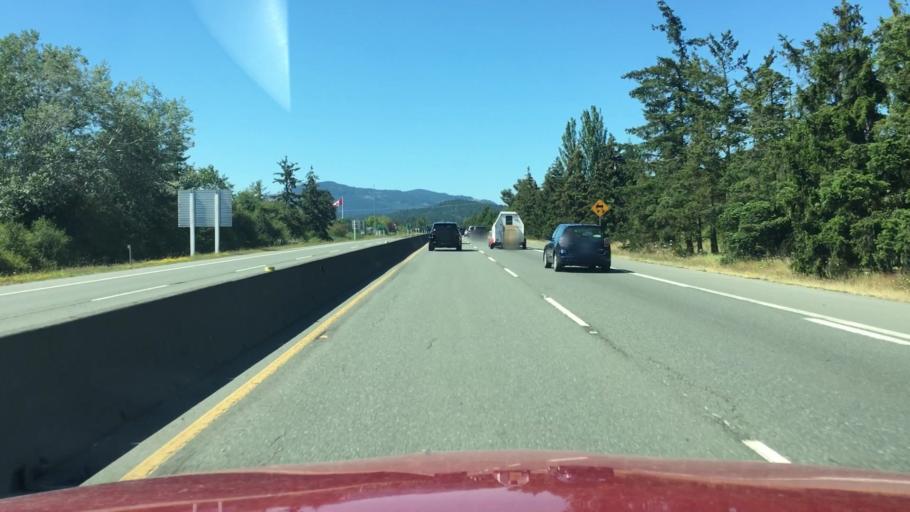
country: CA
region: British Columbia
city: North Saanich
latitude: 48.6517
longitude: -123.4091
